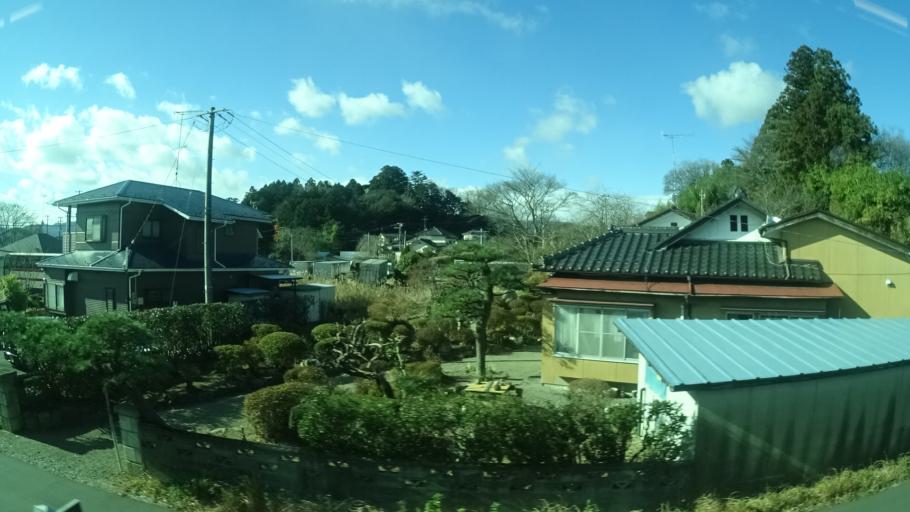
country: JP
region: Miyagi
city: Marumori
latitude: 37.8082
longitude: 140.9239
